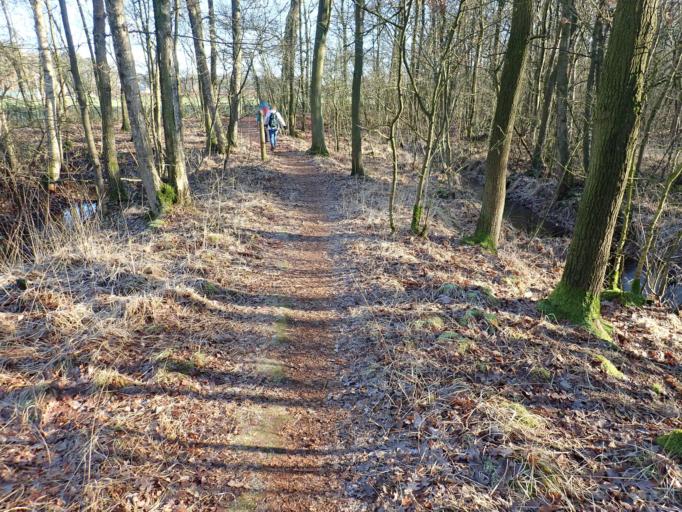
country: BE
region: Flanders
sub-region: Provincie Antwerpen
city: Nijlen
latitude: 51.1610
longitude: 4.6446
